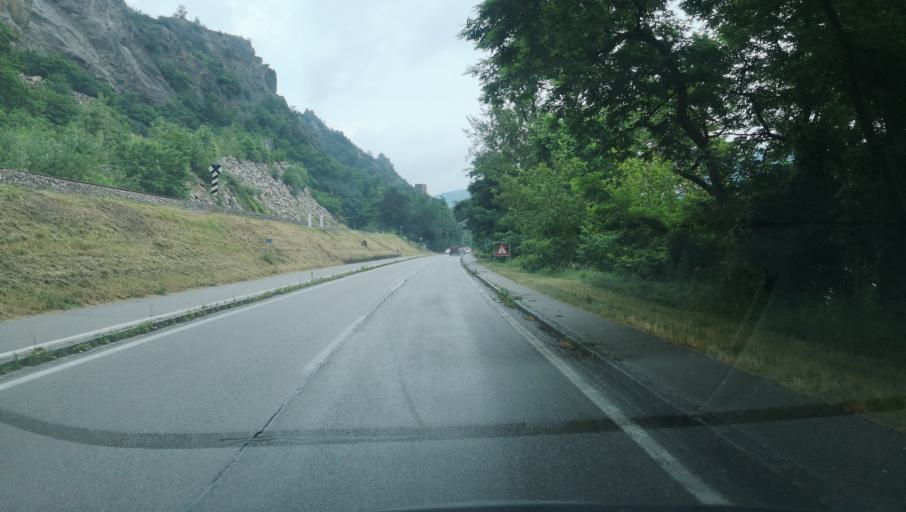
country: AT
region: Lower Austria
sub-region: Politischer Bezirk Krems
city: Durnstein
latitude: 48.4021
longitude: 15.5166
